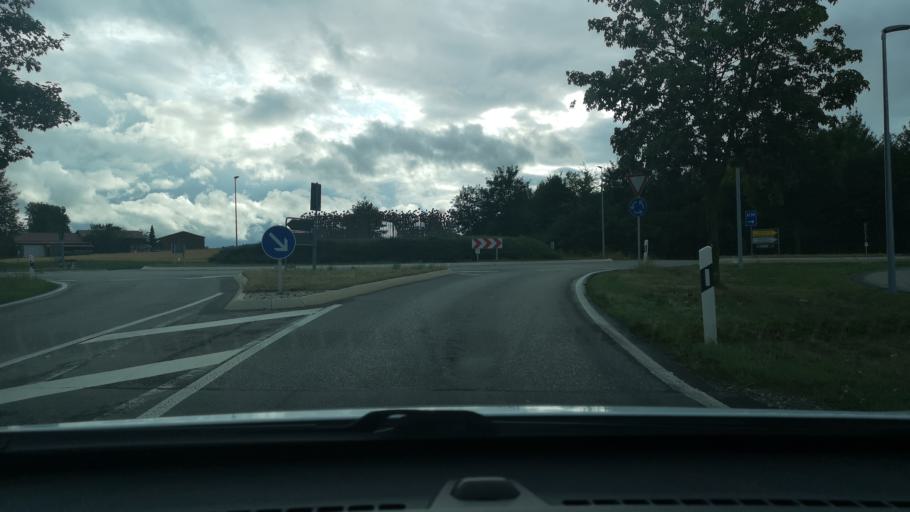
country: DE
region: Baden-Wuerttemberg
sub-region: Freiburg Region
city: Vohringen
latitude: 48.2980
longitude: 8.6273
